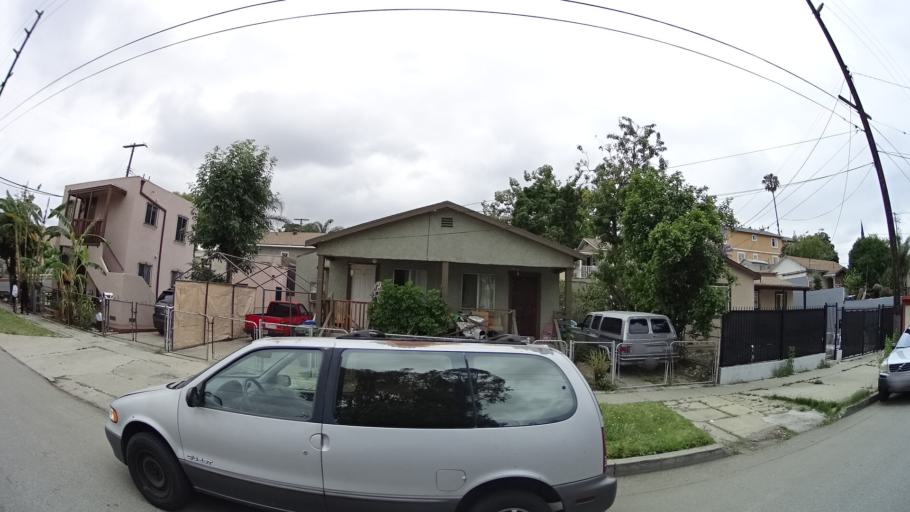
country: US
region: California
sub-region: Los Angeles County
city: Boyle Heights
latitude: 34.0634
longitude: -118.1965
